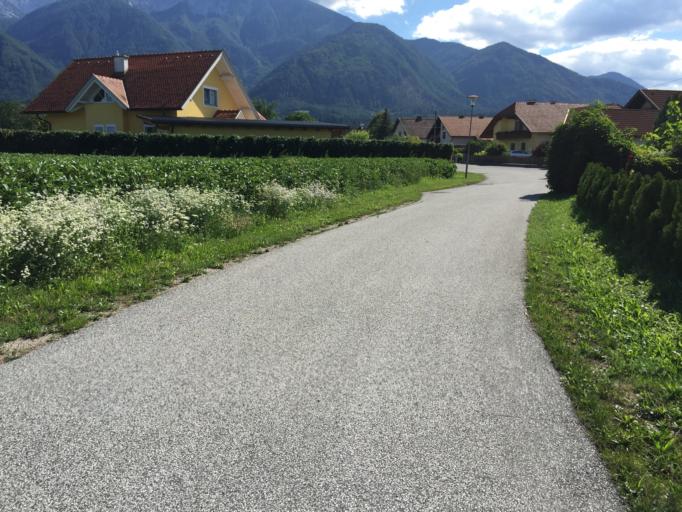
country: AT
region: Carinthia
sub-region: Politischer Bezirk Volkermarkt
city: Feistritz ob Bleiburg
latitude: 46.5634
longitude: 14.7649
